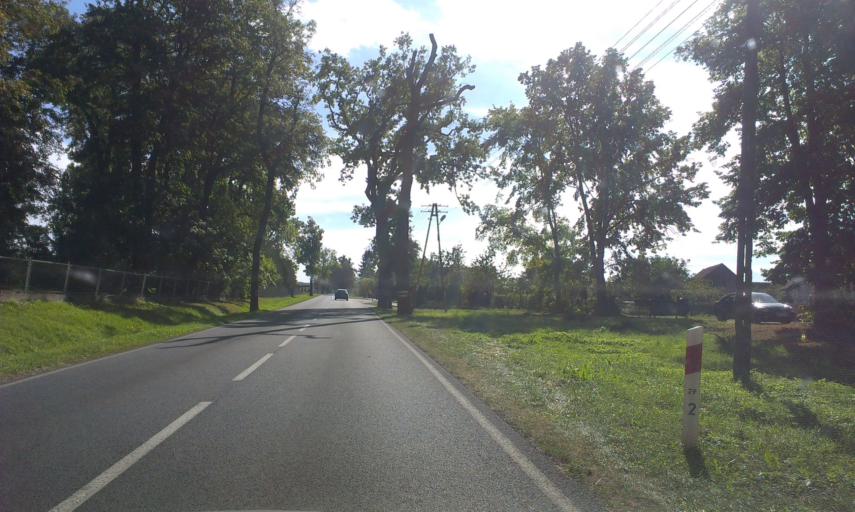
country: PL
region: Greater Poland Voivodeship
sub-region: Powiat pilski
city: Wyrzysk
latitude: 53.1735
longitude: 17.2214
